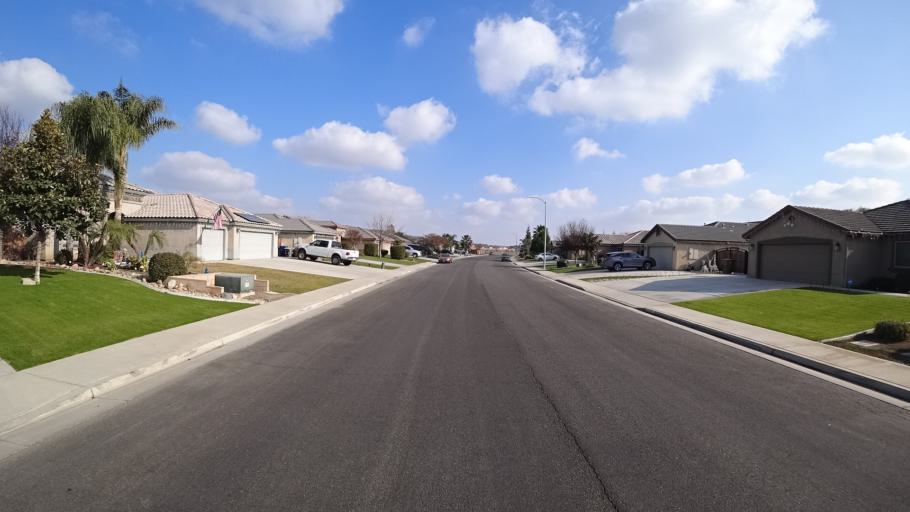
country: US
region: California
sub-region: Kern County
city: Greenacres
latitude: 35.2913
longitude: -119.1087
